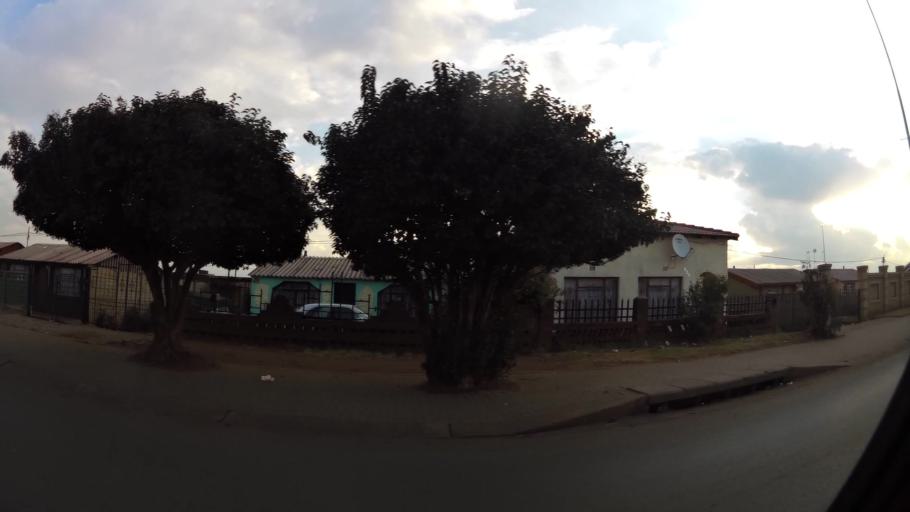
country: ZA
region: Gauteng
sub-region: City of Johannesburg Metropolitan Municipality
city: Orange Farm
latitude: -26.5653
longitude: 27.8347
